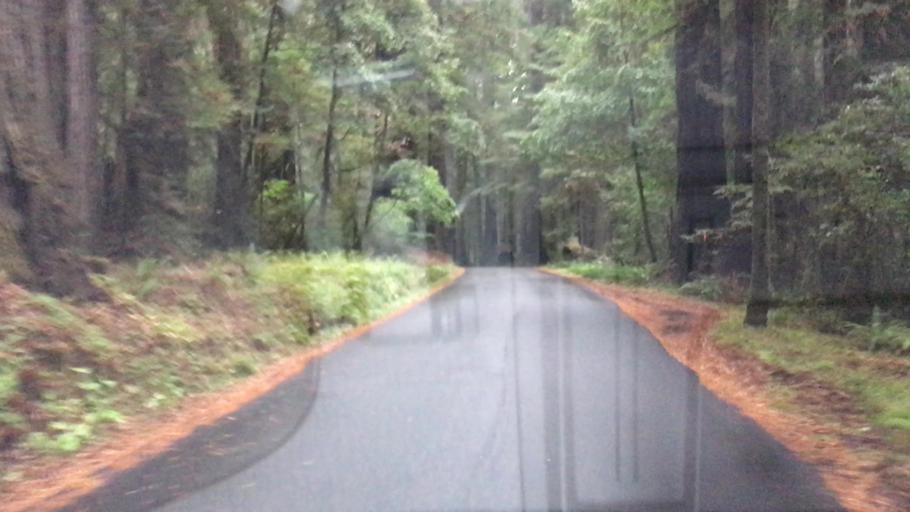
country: US
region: California
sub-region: Humboldt County
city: Rio Dell
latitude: 40.3525
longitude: -123.9743
